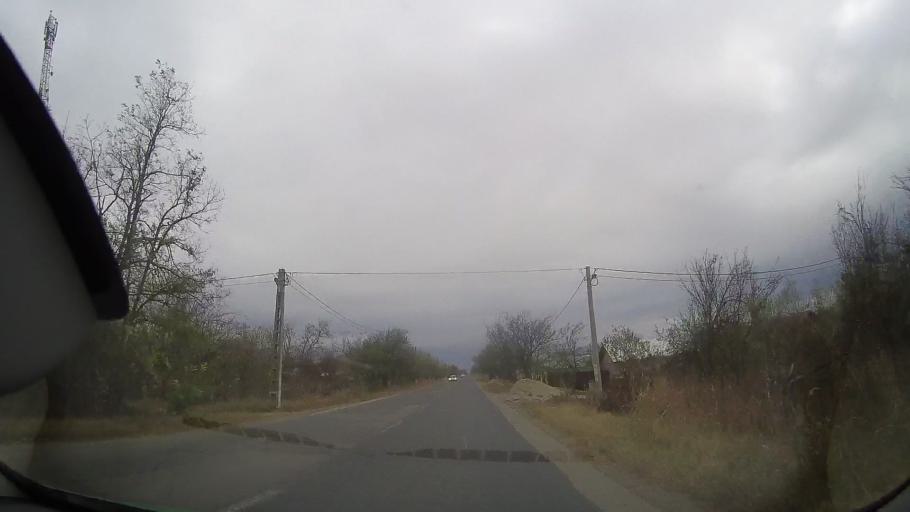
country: RO
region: Buzau
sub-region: Comuna Padina
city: Padina
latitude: 44.7780
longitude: 27.1582
